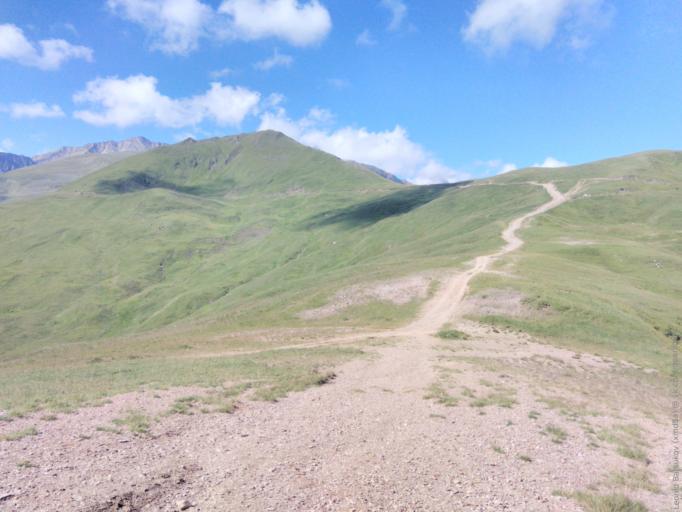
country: RU
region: Kabardino-Balkariya
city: Tyrnyauz
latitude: 43.4246
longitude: 42.8511
